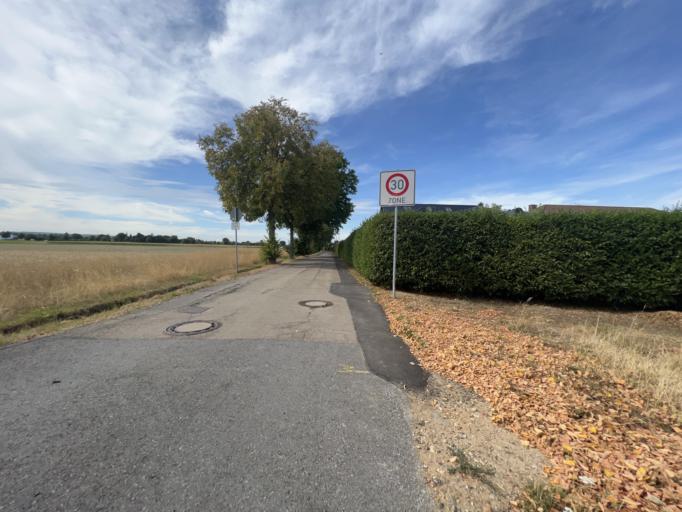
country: DE
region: North Rhine-Westphalia
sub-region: Regierungsbezirk Koln
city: Kreuzau
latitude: 50.7743
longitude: 6.4674
